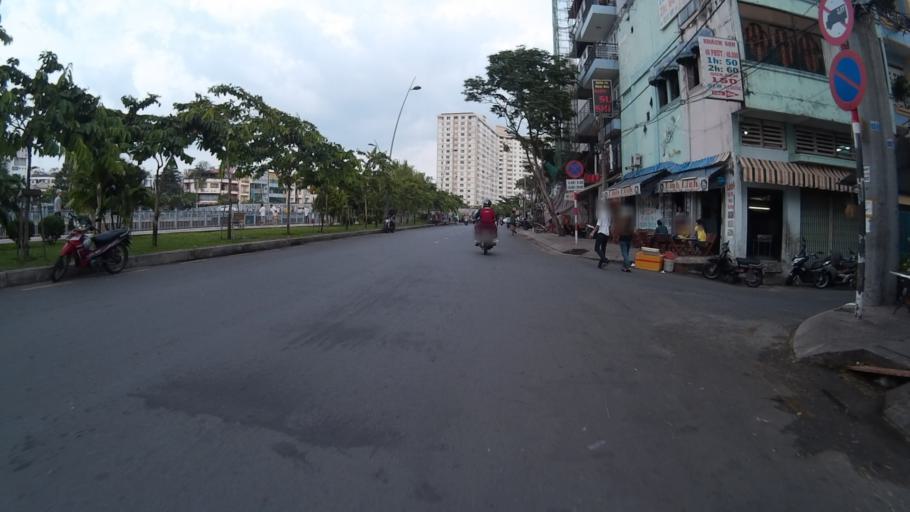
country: VN
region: Ho Chi Minh City
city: Quan Binh Thanh
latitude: 10.7952
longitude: 106.6898
